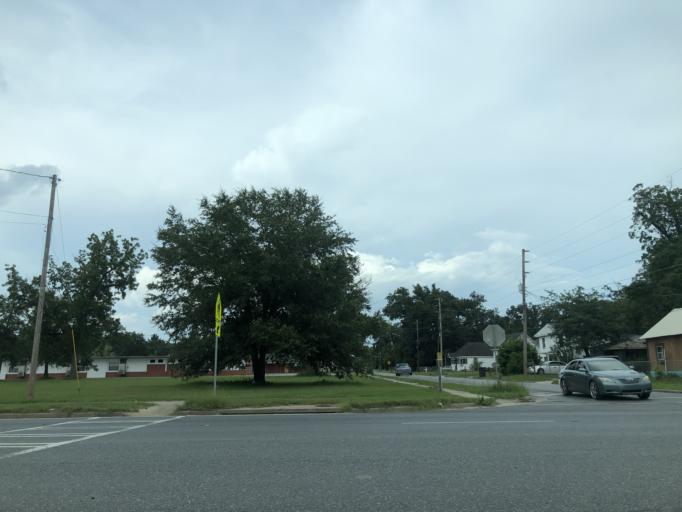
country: US
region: Georgia
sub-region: Wayne County
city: Jesup
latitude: 31.6119
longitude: -81.8864
